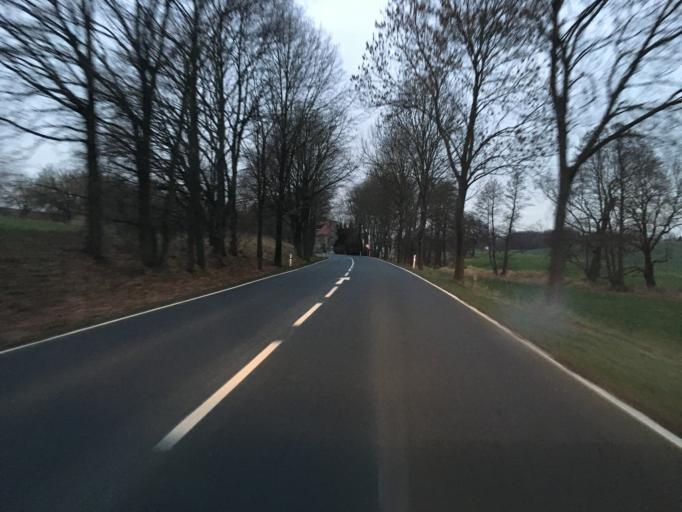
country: DE
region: Saxony
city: Dahlen
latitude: 51.3263
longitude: 13.0249
